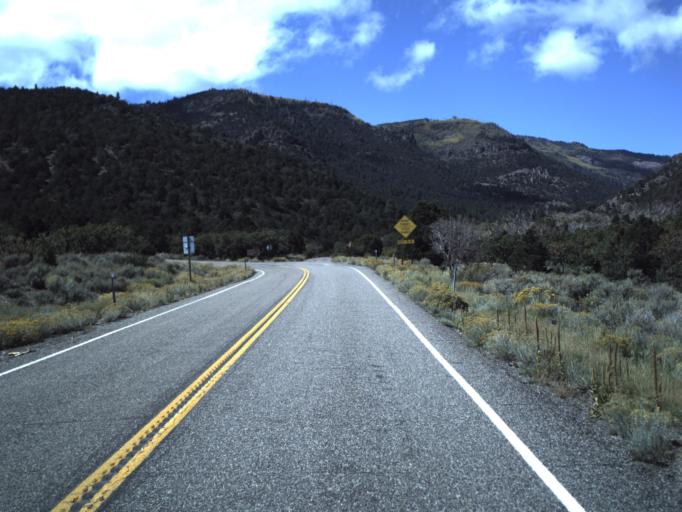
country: US
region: Utah
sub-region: Piute County
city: Junction
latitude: 38.2650
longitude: -112.3032
